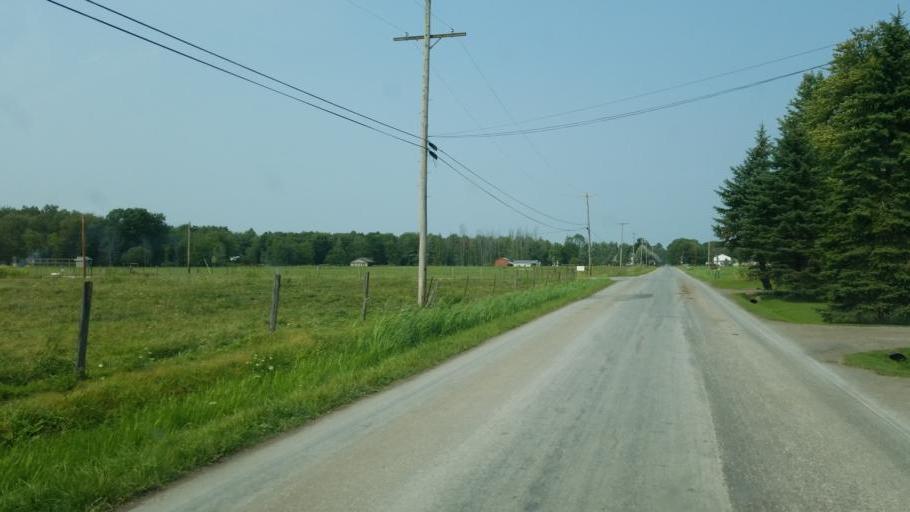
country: US
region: Ohio
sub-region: Geauga County
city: Middlefield
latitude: 41.4932
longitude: -81.0032
